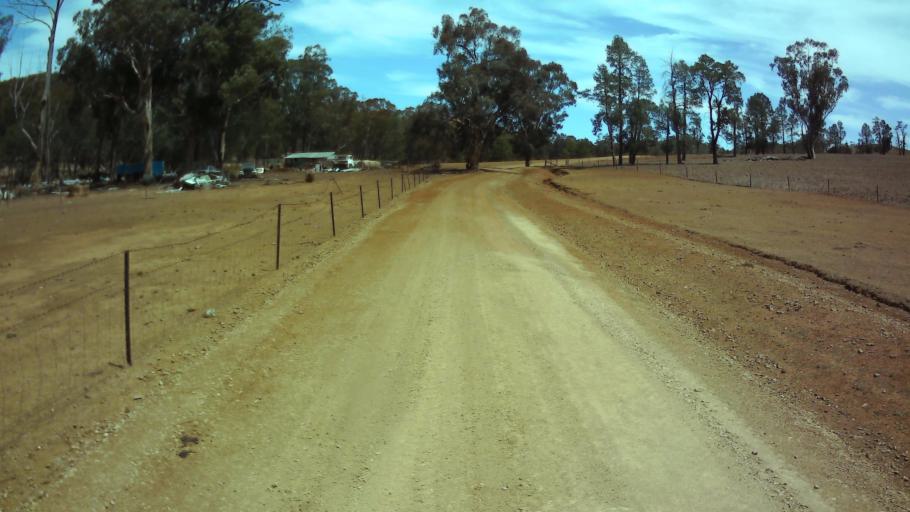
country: AU
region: New South Wales
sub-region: Weddin
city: Grenfell
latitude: -33.7929
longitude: 148.1602
